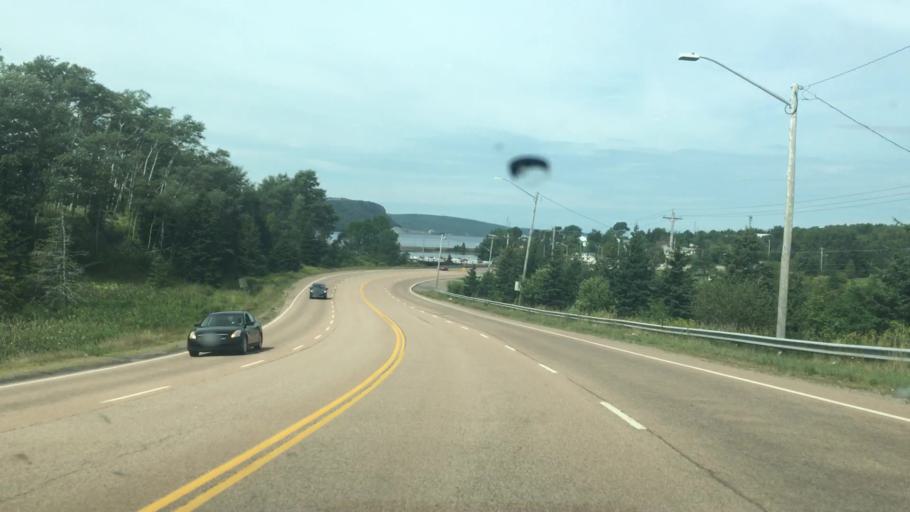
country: CA
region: Nova Scotia
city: Port Hawkesbury
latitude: 45.6208
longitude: -61.3612
